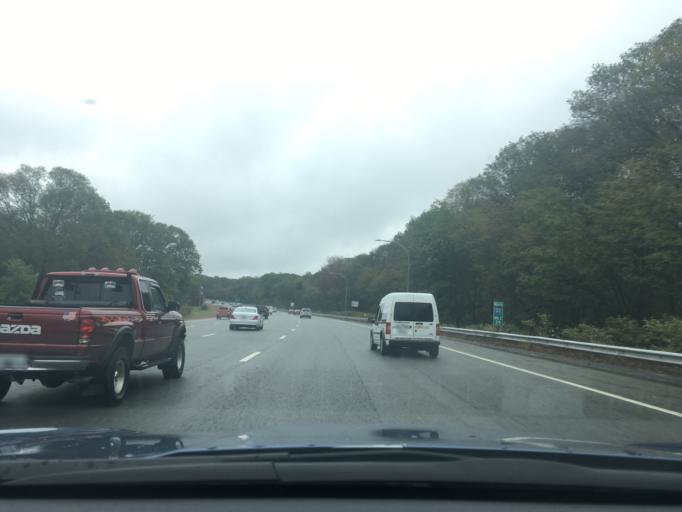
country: US
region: Rhode Island
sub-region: Kent County
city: East Greenwich
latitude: 41.6687
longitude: -71.4832
